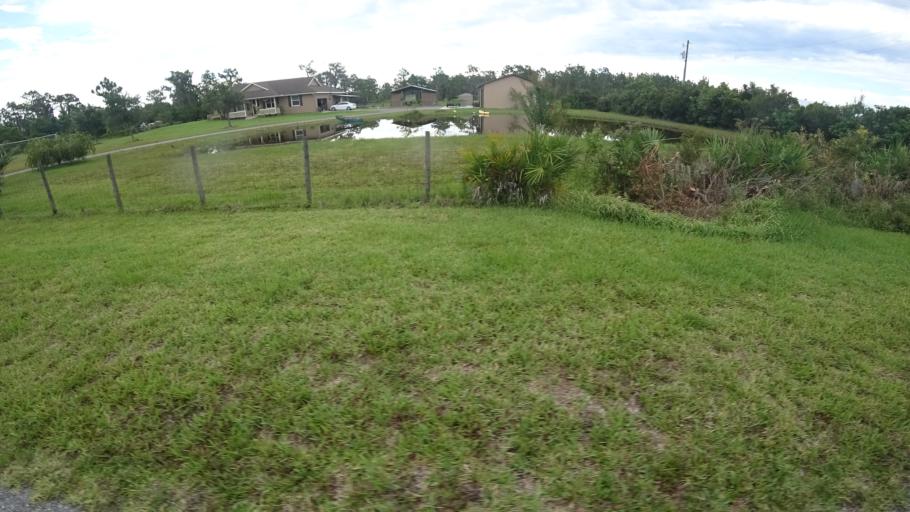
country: US
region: Florida
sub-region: Sarasota County
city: The Meadows
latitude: 27.4115
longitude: -82.2833
